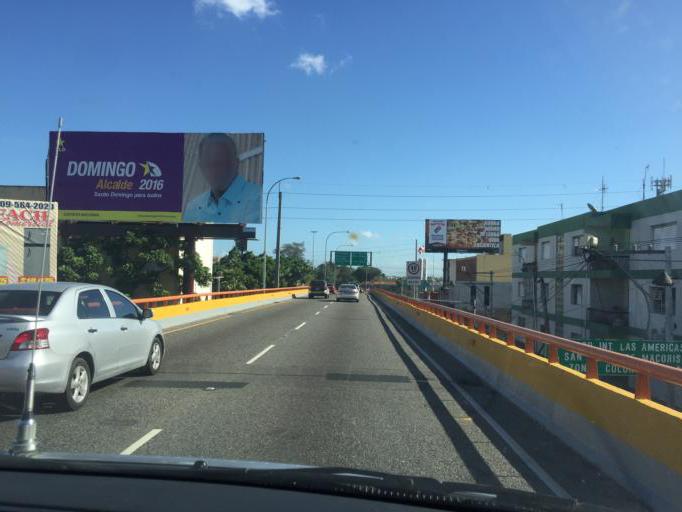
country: DO
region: Nacional
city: San Carlos
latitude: 18.4855
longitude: -69.8889
